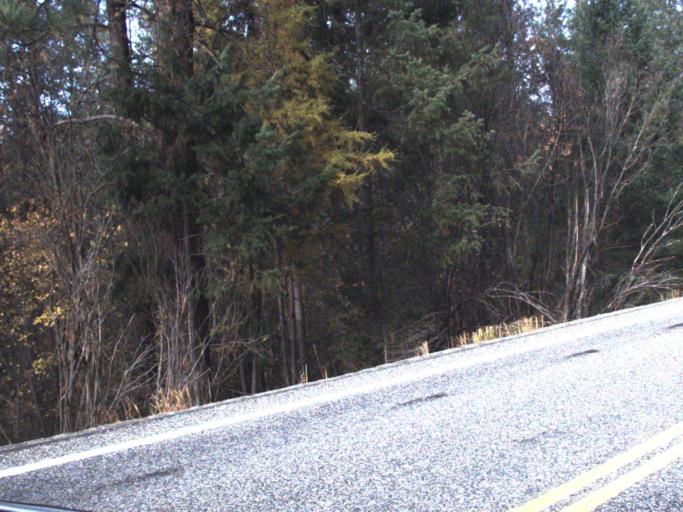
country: US
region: Washington
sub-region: Stevens County
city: Kettle Falls
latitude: 48.8082
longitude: -117.9984
